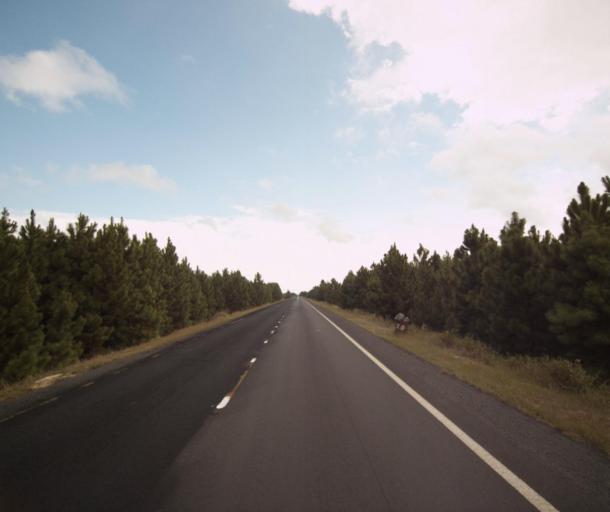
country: BR
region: Rio Grande do Sul
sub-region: Tapes
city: Tapes
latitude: -31.4207
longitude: -51.1789
